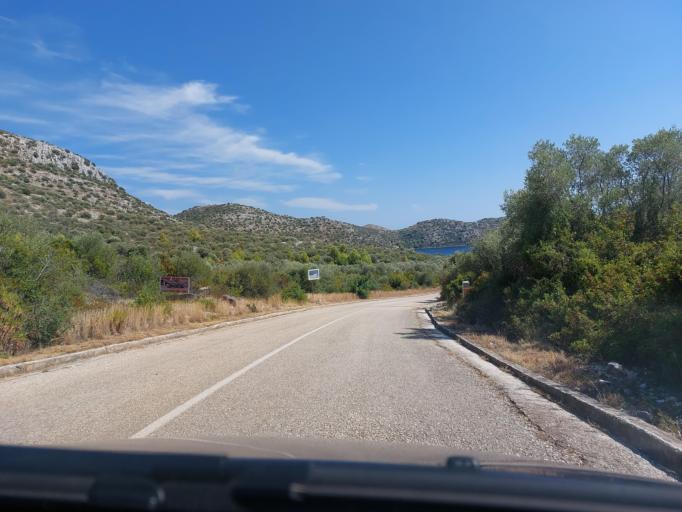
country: HR
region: Dubrovacko-Neretvanska
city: Smokvica
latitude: 42.7433
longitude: 16.8834
